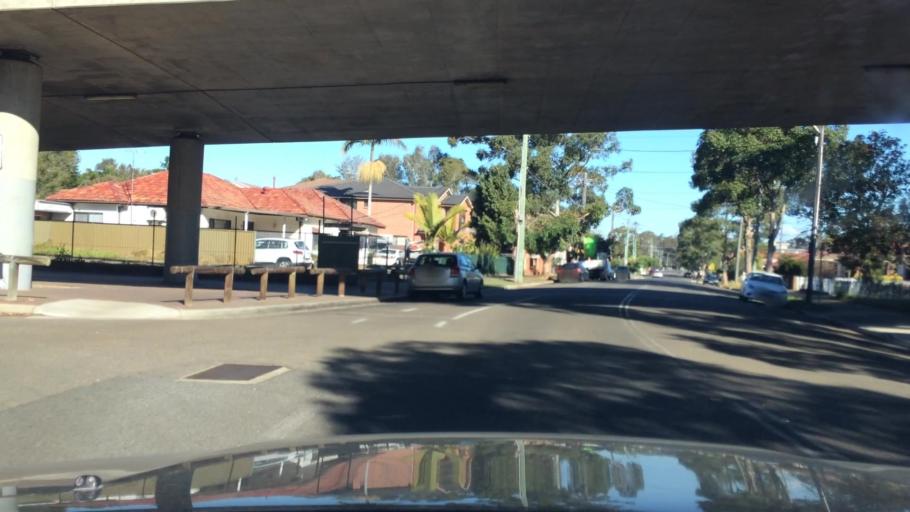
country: AU
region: New South Wales
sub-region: Fairfield
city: Carramar
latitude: -33.8737
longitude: 150.9563
